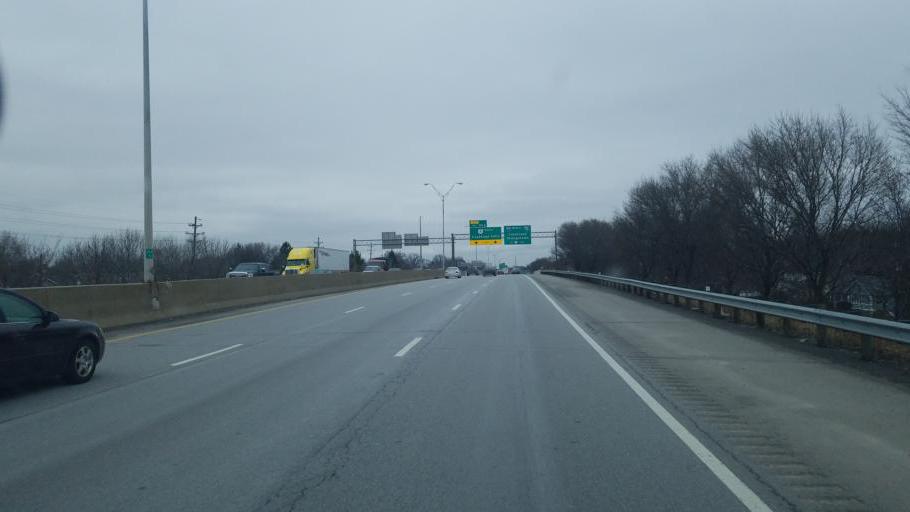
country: US
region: Ohio
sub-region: Summit County
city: Akron
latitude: 41.0448
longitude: -81.5054
